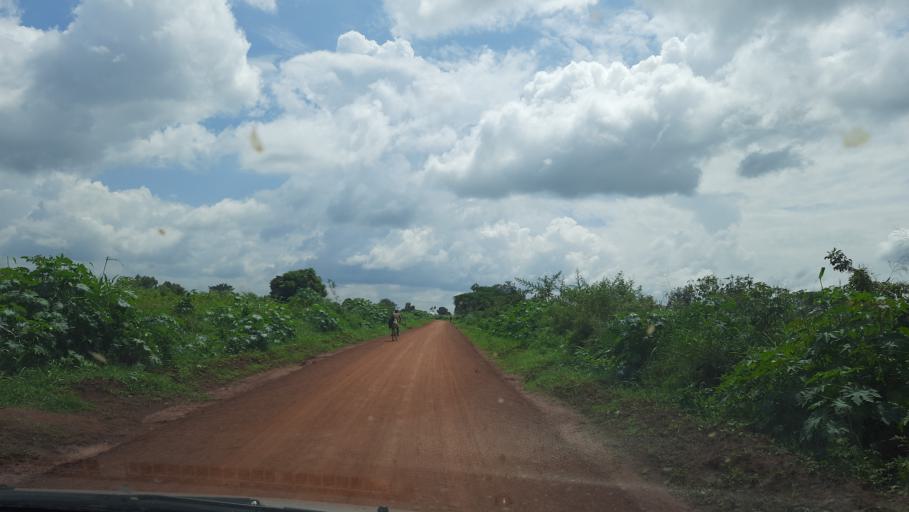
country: UG
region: Western Region
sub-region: Kiryandongo District
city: Kiryandongo
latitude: 1.8238
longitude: 31.9828
